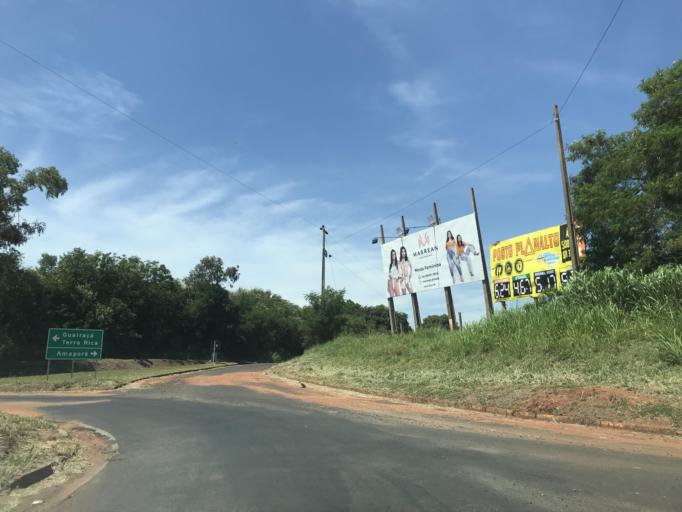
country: BR
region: Parana
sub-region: Paranavai
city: Nova Aurora
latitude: -22.9542
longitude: -52.7016
